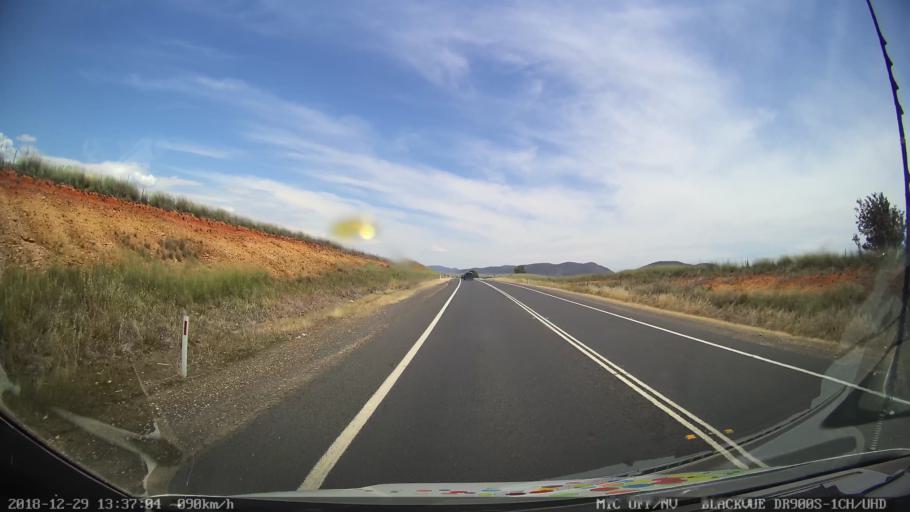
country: AU
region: New South Wales
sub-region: Cooma-Monaro
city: Cooma
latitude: -35.9783
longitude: 149.1375
